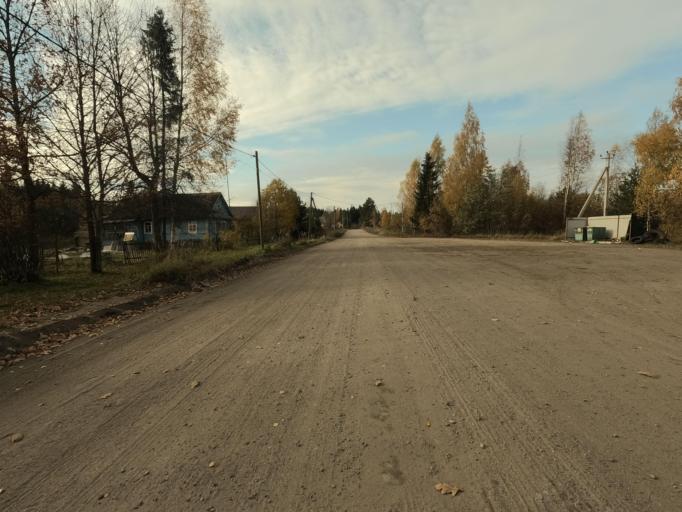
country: RU
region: Leningrad
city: Priladozhskiy
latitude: 59.6300
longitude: 31.4023
